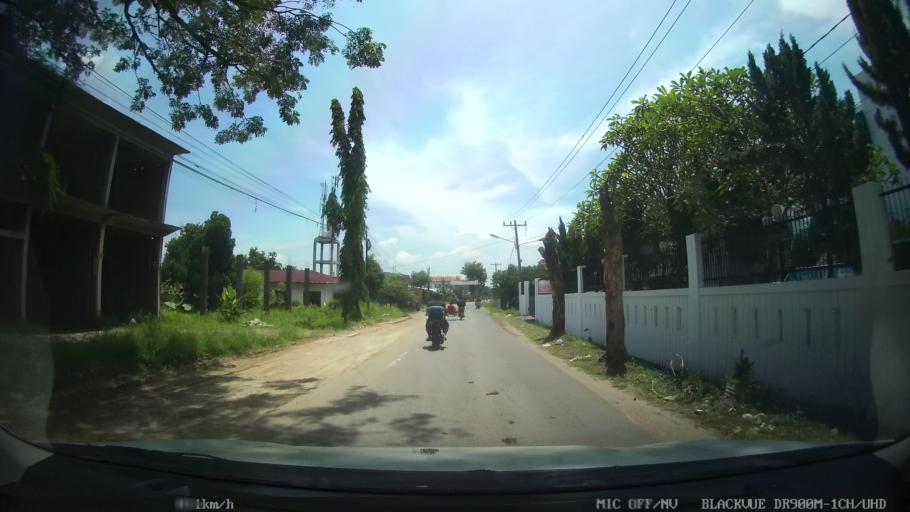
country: ID
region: North Sumatra
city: Binjai
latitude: 3.5941
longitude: 98.4910
